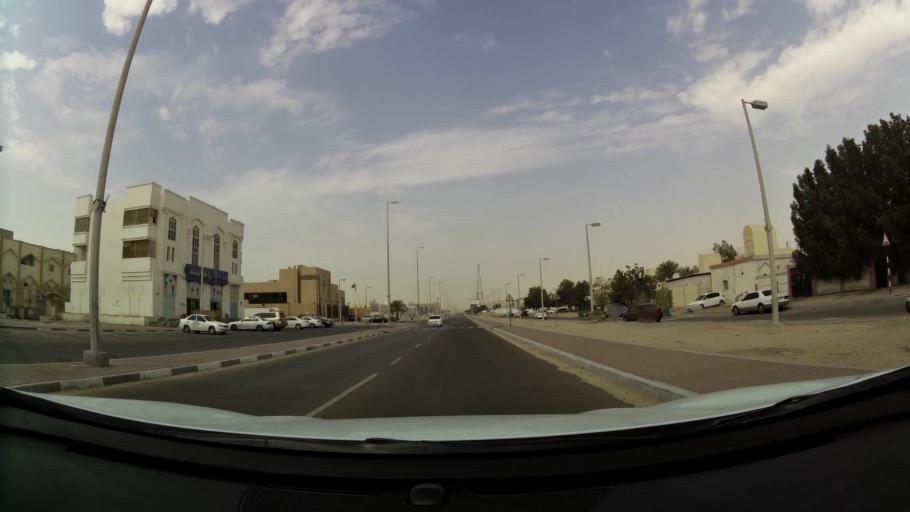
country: AE
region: Abu Dhabi
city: Abu Dhabi
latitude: 24.3068
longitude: 54.6121
